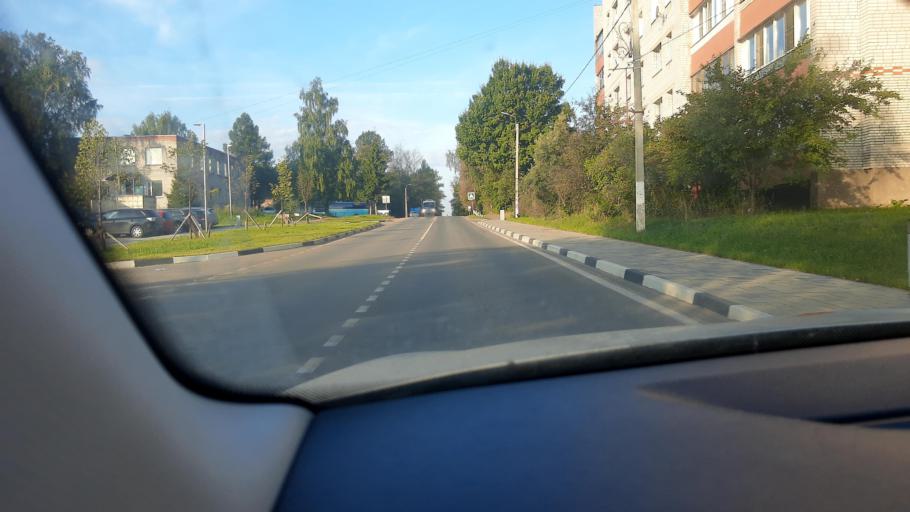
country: RU
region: Moskovskaya
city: Selyatino
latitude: 55.5588
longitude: 36.9788
